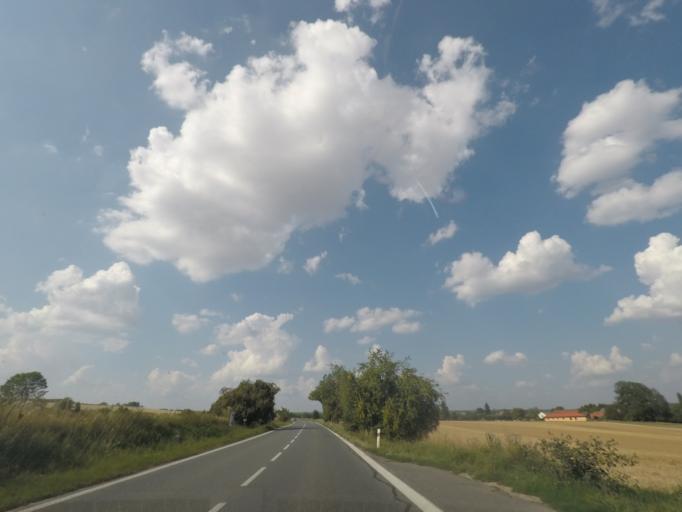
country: CZ
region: Kralovehradecky
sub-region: Okres Nachod
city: Jaromer
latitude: 50.3665
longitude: 15.9069
